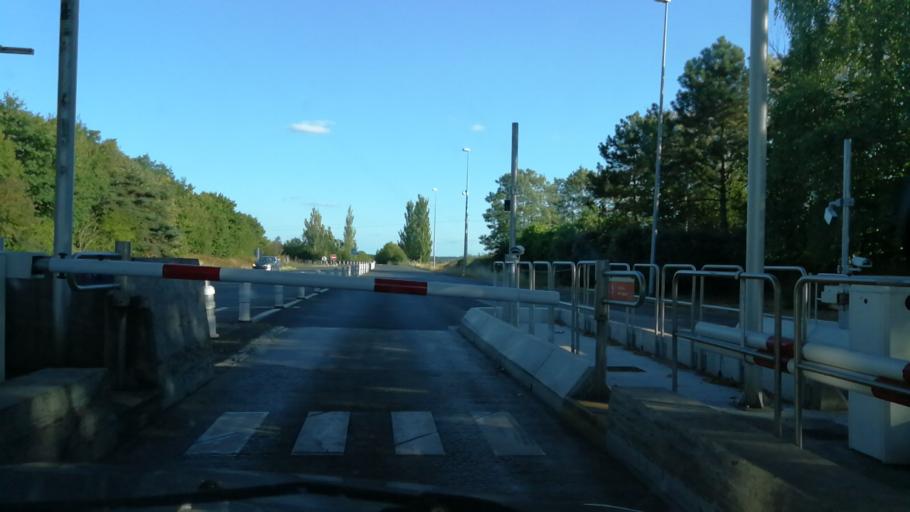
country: FR
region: Centre
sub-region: Departement d'Indre-et-Loire
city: Sainte-Maure-de-Touraine
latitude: 47.1074
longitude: 0.5876
